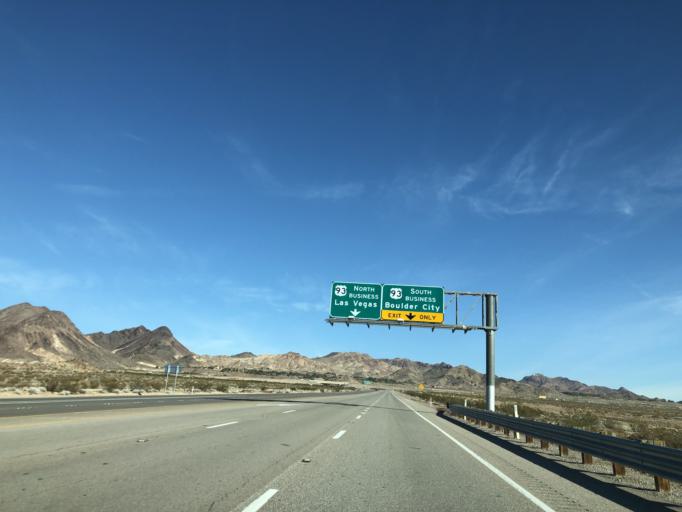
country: US
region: Nevada
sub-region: Clark County
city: Boulder City
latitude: 35.9591
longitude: -114.8982
